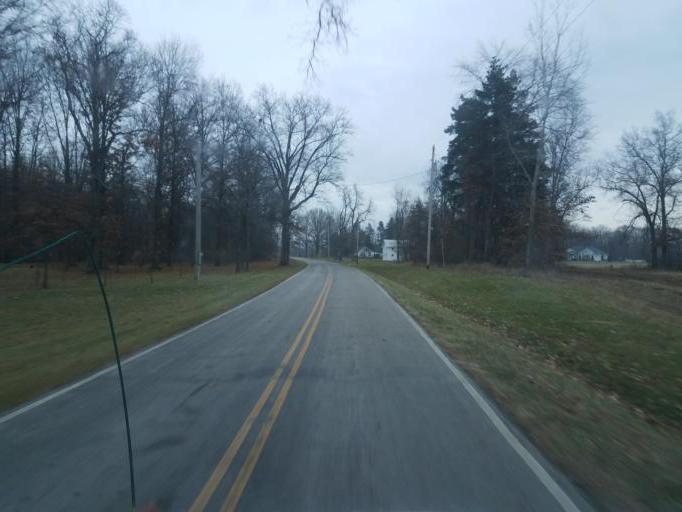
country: US
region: Ohio
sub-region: Morrow County
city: Cardington
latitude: 40.5565
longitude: -83.0037
